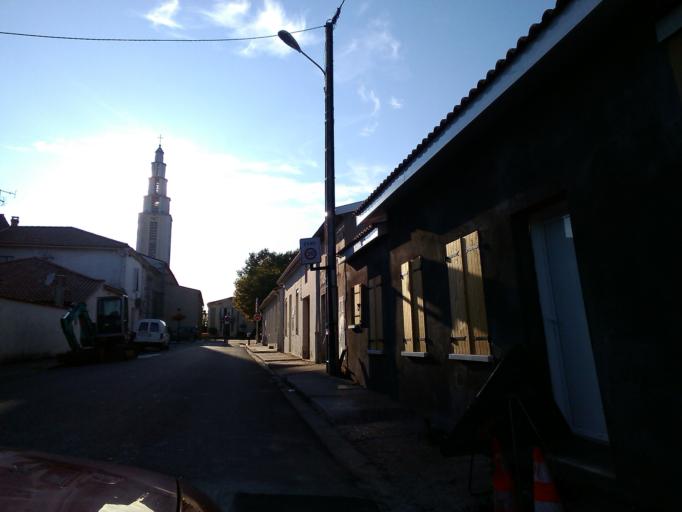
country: FR
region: Aquitaine
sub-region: Departement de la Gironde
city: Soulac-sur-Mer
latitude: 45.4306
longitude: -1.0344
